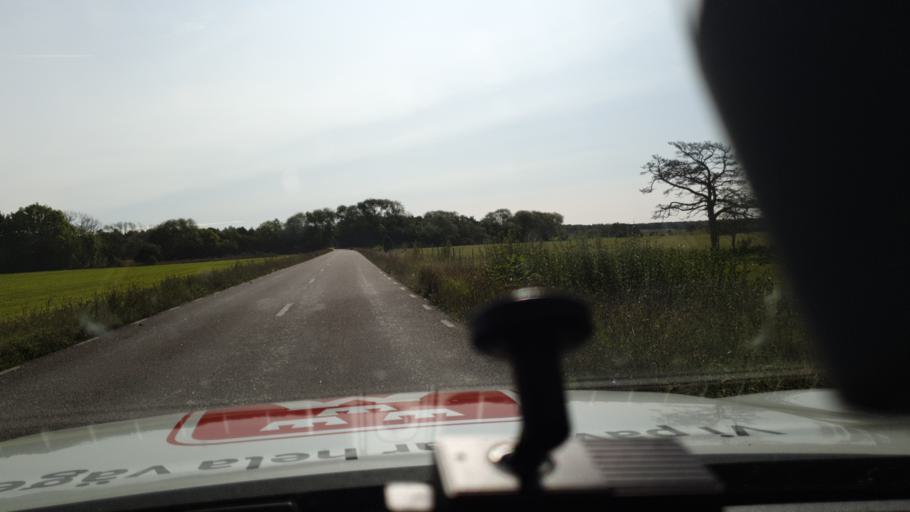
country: SE
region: Gotland
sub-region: Gotland
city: Hemse
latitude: 57.1081
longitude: 18.2927
